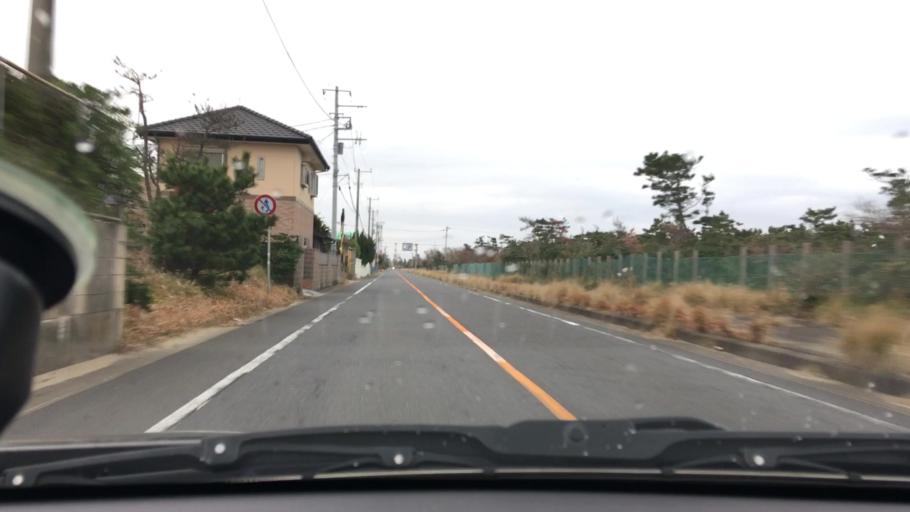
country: JP
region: Chiba
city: Omigawa
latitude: 35.8662
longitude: 140.7395
